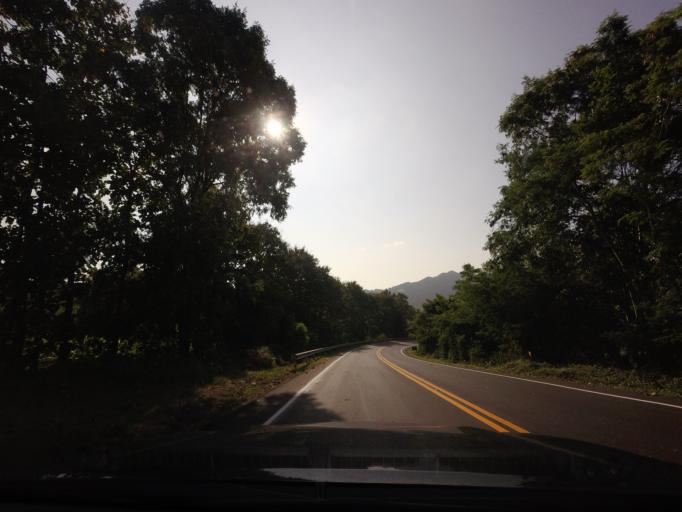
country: TH
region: Phetchabun
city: Lom Kao
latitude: 16.8732
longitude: 101.1320
